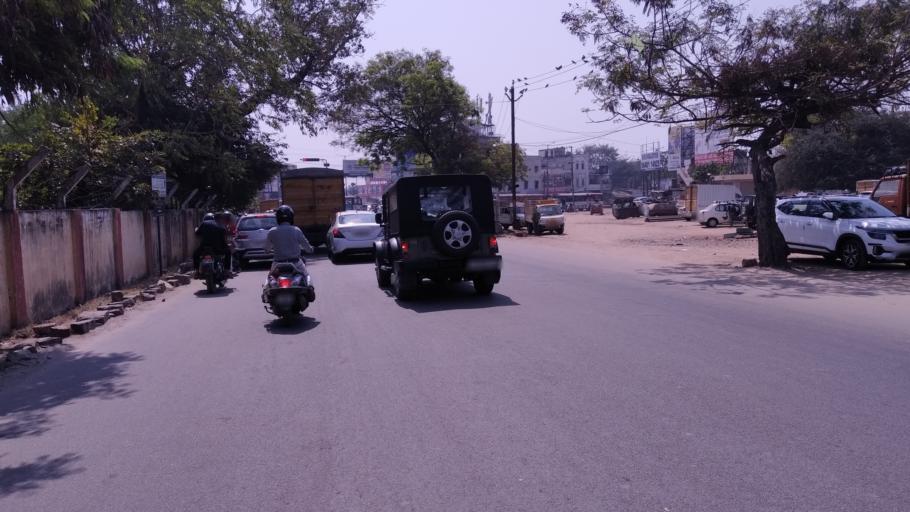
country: IN
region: Telangana
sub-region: Hyderabad
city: Malkajgiri
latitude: 17.4579
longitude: 78.4850
